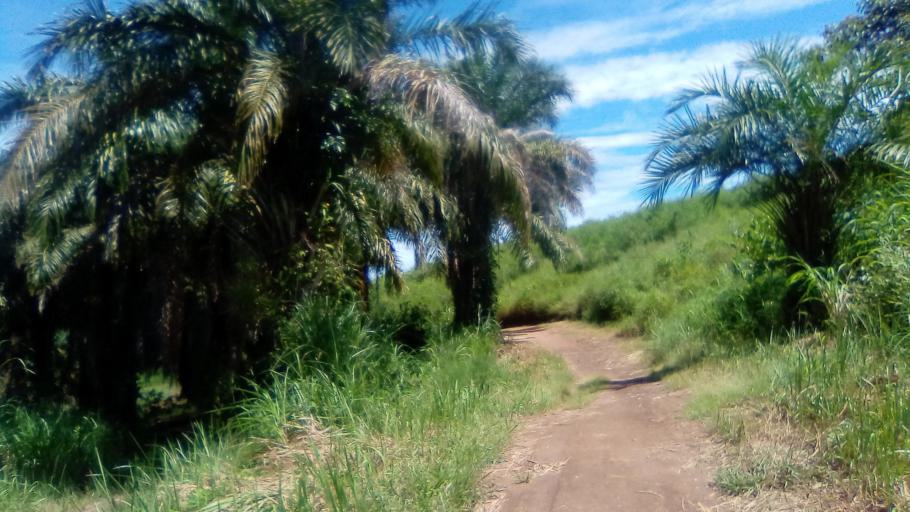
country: SL
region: Eastern Province
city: Simbakoro
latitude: 8.6314
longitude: -10.9957
